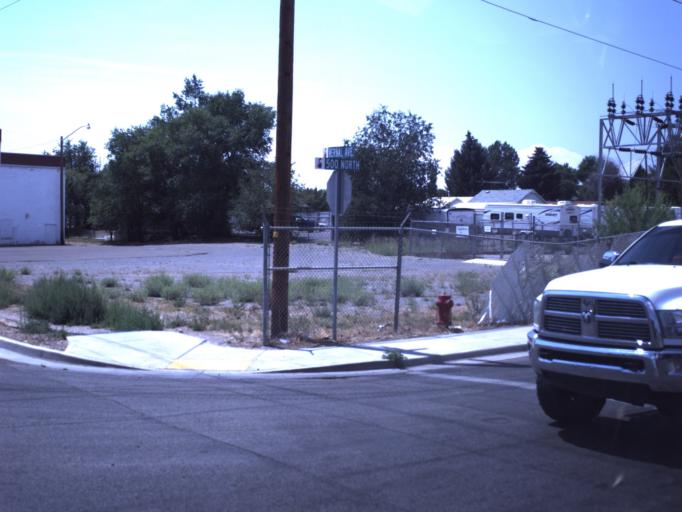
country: US
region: Utah
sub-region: Uintah County
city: Vernal
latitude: 40.4630
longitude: -109.5288
